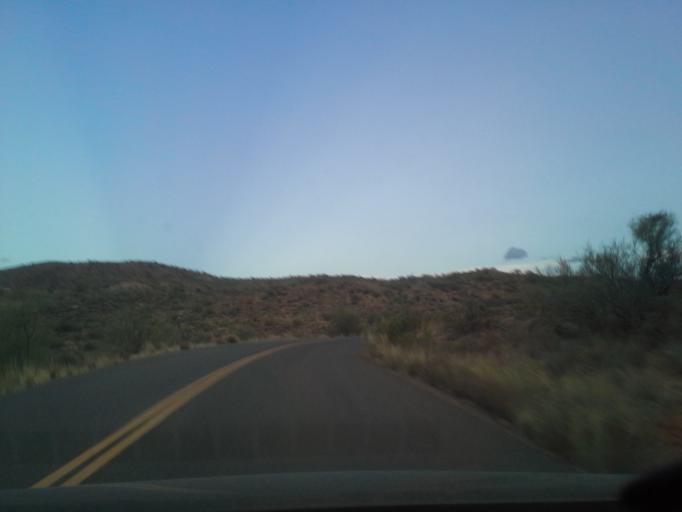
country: US
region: Arizona
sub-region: Yavapai County
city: Black Canyon City
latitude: 34.1526
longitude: -112.1539
